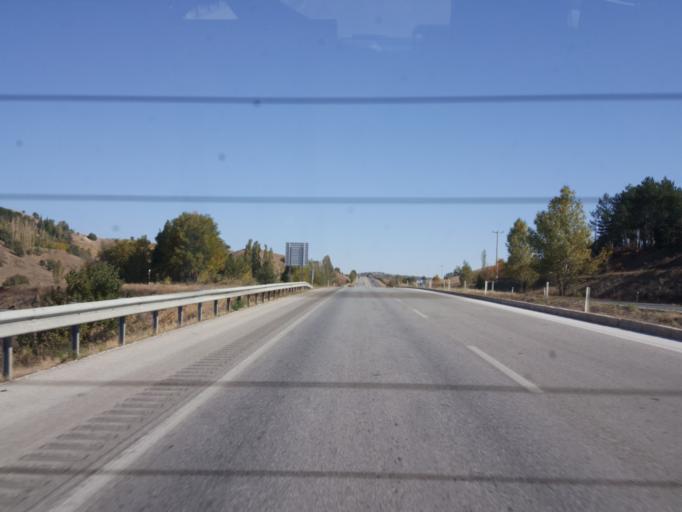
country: TR
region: Corum
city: Alaca
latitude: 40.2789
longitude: 34.6441
